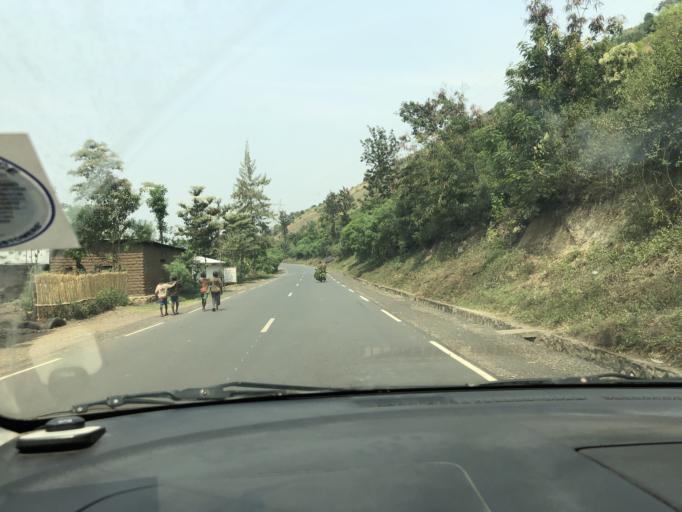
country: BI
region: Cibitoke
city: Cibitoke
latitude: -2.6943
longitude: 29.0034
